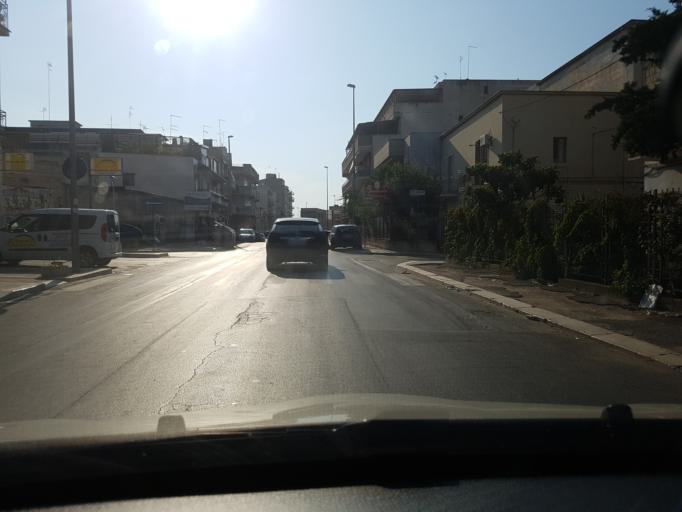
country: IT
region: Apulia
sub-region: Provincia di Foggia
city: Cerignola
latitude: 41.2685
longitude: 15.9029
